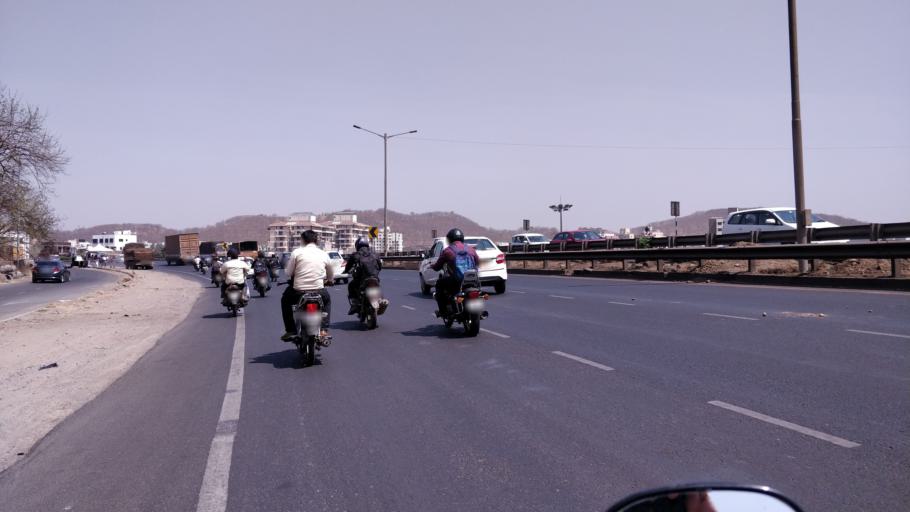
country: IN
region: Maharashtra
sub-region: Pune Division
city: Shivaji Nagar
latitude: 18.5384
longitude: 73.7810
